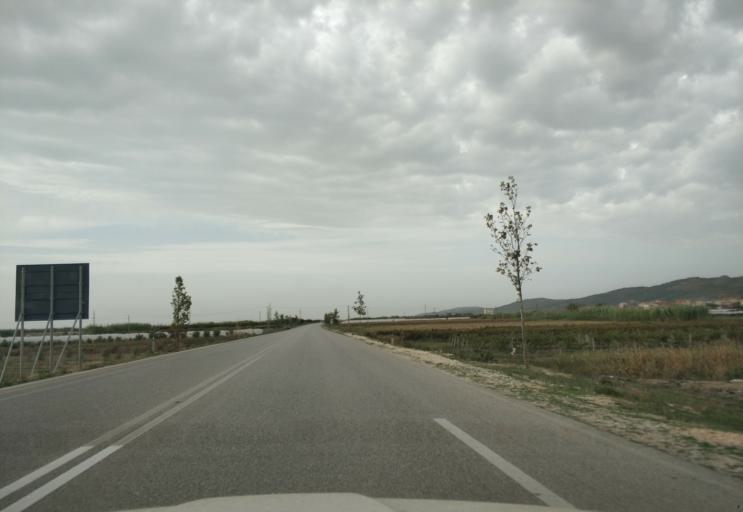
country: AL
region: Fier
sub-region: Rrethi i Fierit
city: Frakulla e Madhe
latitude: 40.6318
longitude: 19.5079
